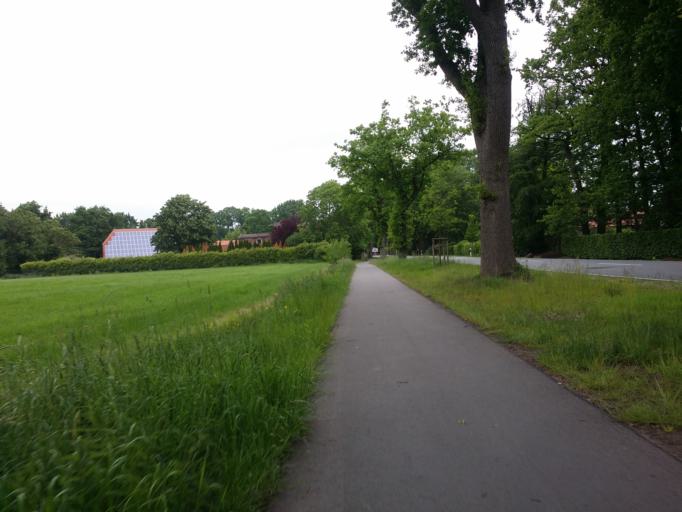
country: DE
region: Lower Saxony
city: Rastede
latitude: 53.2117
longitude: 8.2486
